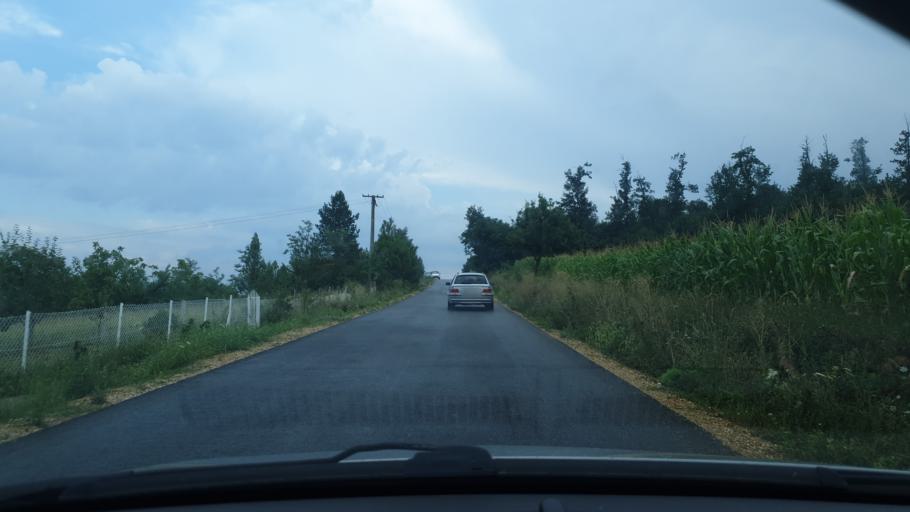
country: RS
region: Central Serbia
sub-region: Sumadijski Okrug
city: Kragujevac
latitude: 44.0606
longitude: 20.7848
